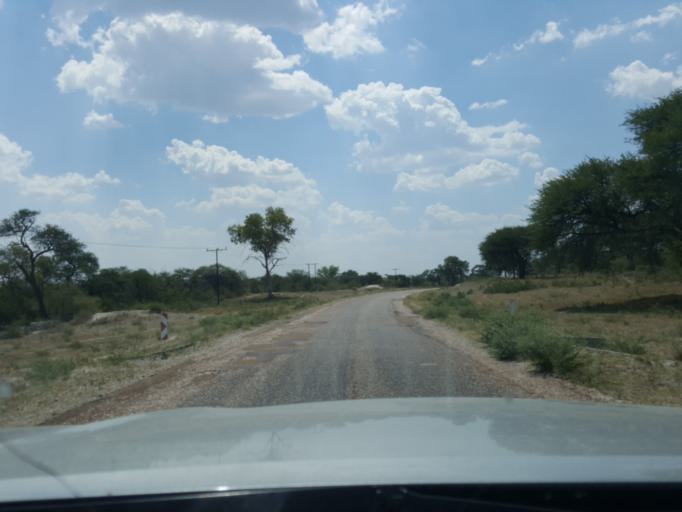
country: BW
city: Tsau
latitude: -19.9787
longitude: 22.2540
